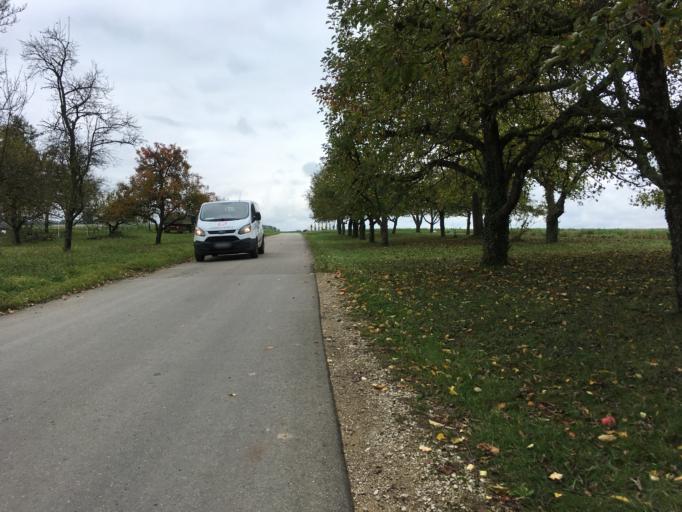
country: DE
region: Baden-Wuerttemberg
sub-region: Tuebingen Region
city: Gomaringen
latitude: 48.4812
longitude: 9.0991
